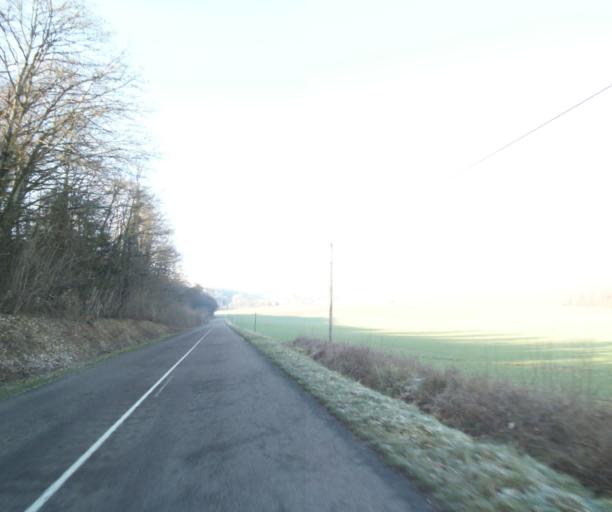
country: FR
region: Champagne-Ardenne
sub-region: Departement de la Haute-Marne
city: Chevillon
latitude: 48.5500
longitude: 5.0947
